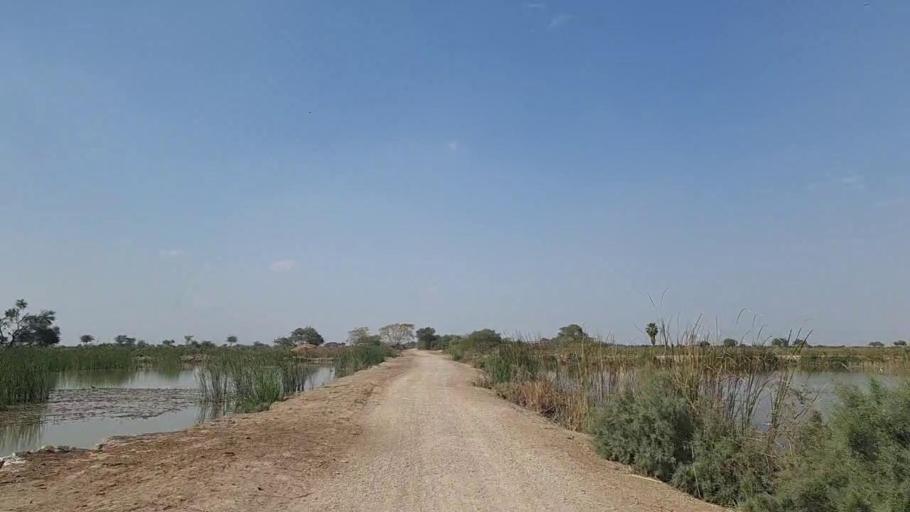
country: PK
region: Sindh
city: Jati
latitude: 24.5109
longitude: 68.2953
